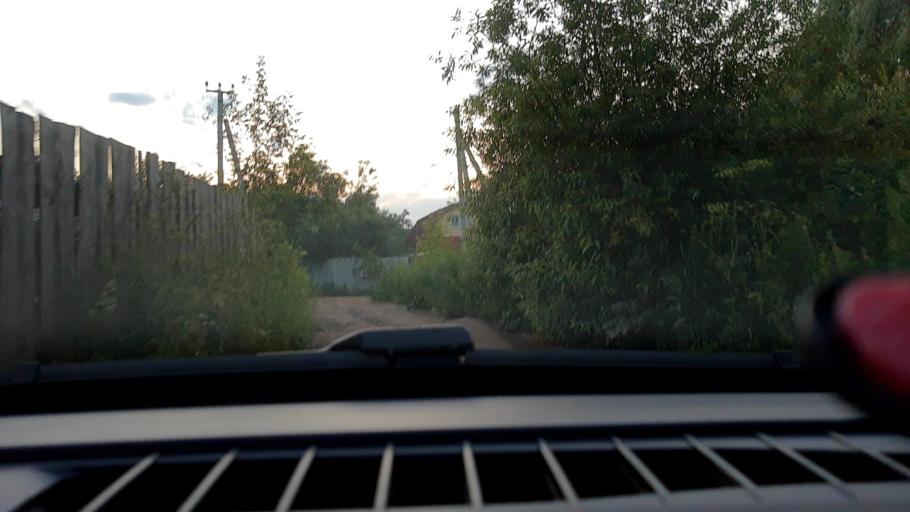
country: RU
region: Nizjnij Novgorod
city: Afonino
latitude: 56.2524
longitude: 44.0721
